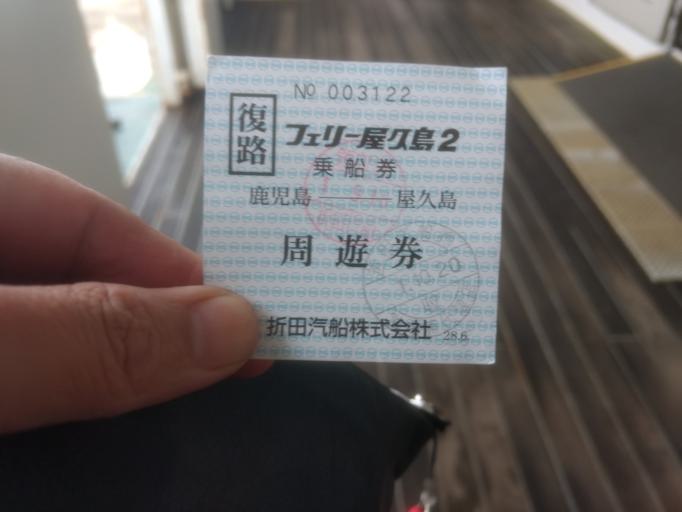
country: JP
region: Kagoshima
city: Nishinoomote
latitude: 30.4322
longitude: 130.5736
